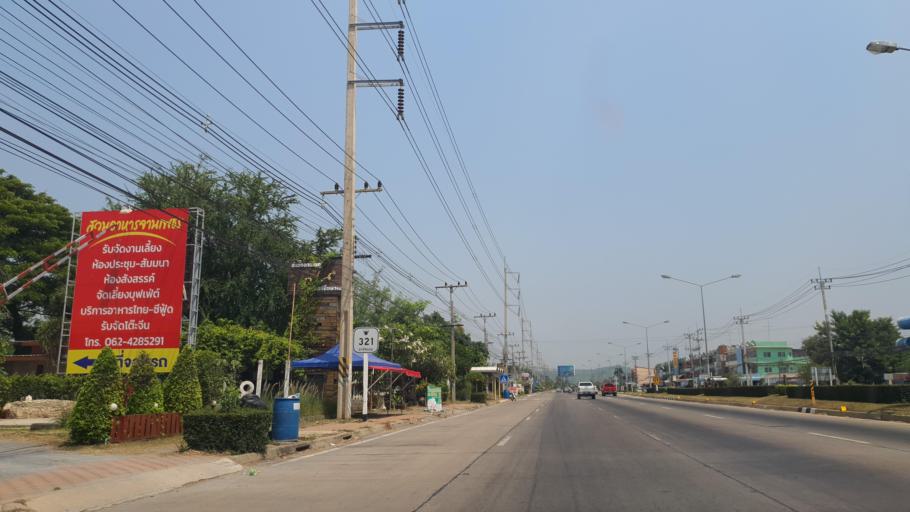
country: TH
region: Suphan Buri
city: U Thong
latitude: 14.3199
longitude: 99.8639
